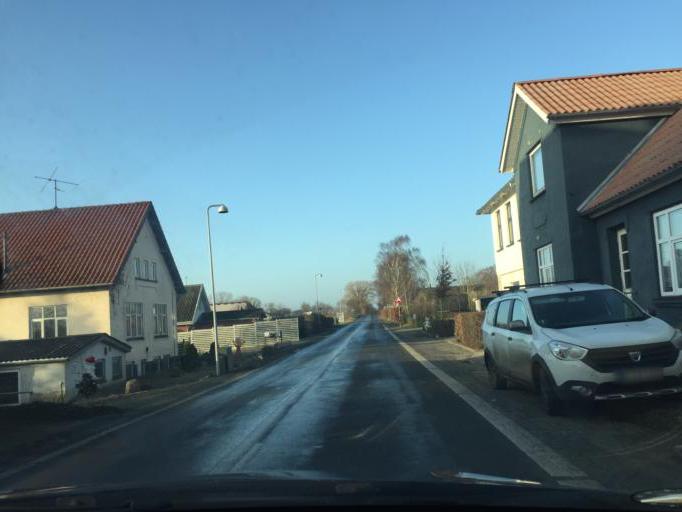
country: DK
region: South Denmark
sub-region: Faaborg-Midtfyn Kommune
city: Ringe
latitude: 55.1931
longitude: 10.3469
